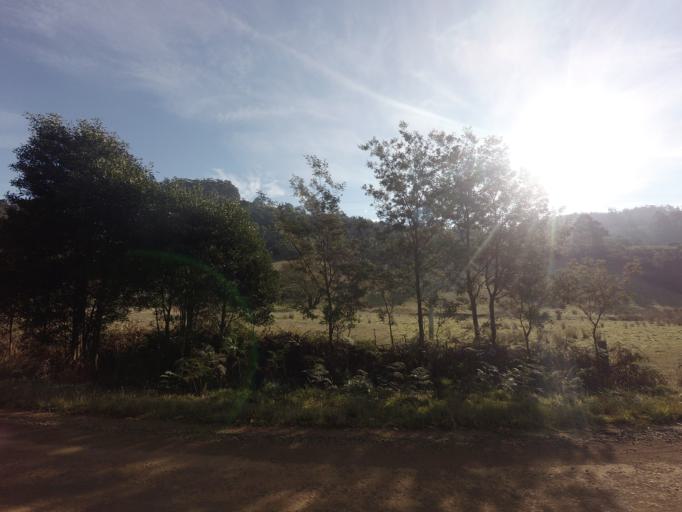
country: AU
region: Tasmania
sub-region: Sorell
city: Sorell
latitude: -42.5049
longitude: 147.4299
